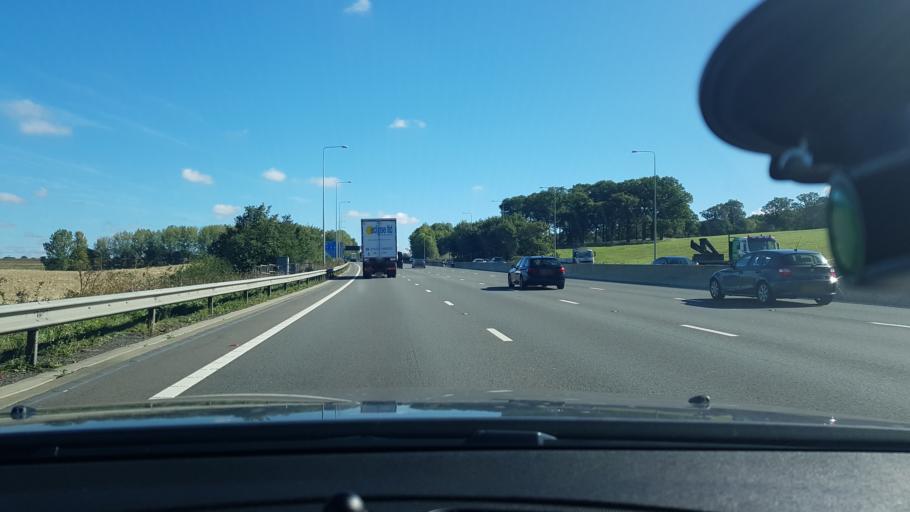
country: GB
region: England
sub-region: Essex
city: Theydon Bois
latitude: 51.6889
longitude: 0.0803
